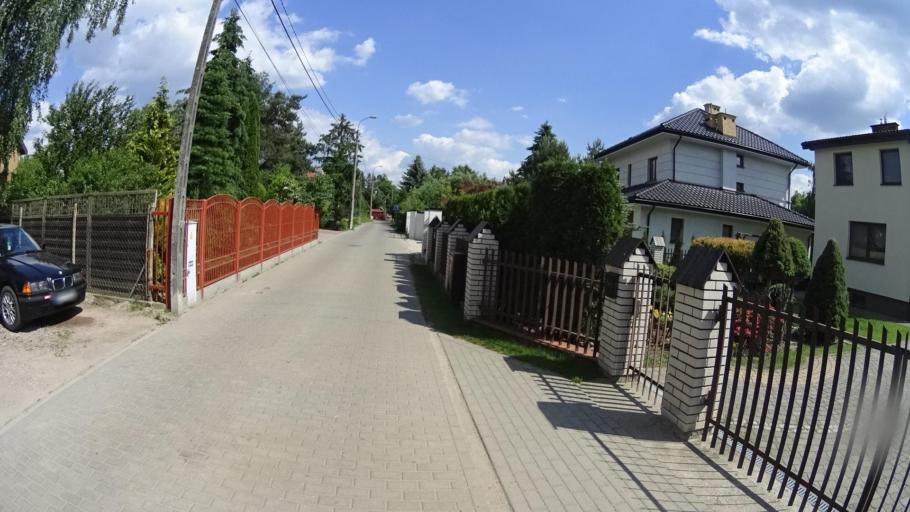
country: PL
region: Masovian Voivodeship
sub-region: Powiat piaseczynski
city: Konstancin-Jeziorna
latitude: 52.0925
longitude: 21.1100
